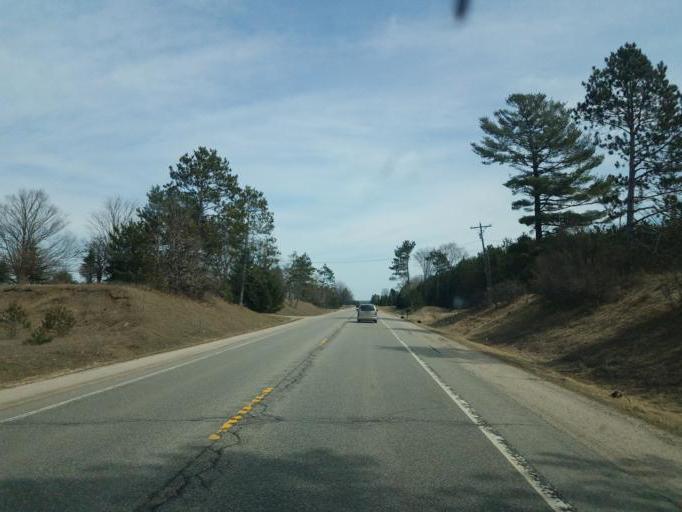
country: US
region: Michigan
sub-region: Osceola County
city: Reed City
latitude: 43.8877
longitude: -85.5511
